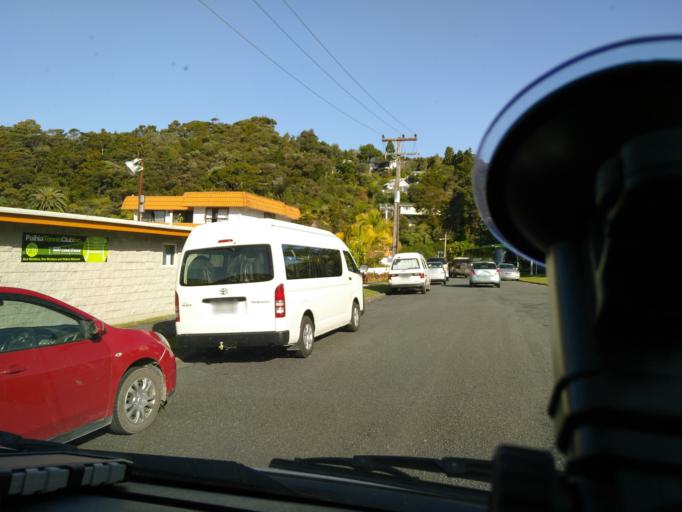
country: NZ
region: Northland
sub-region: Far North District
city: Paihia
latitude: -35.2866
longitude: 174.0948
